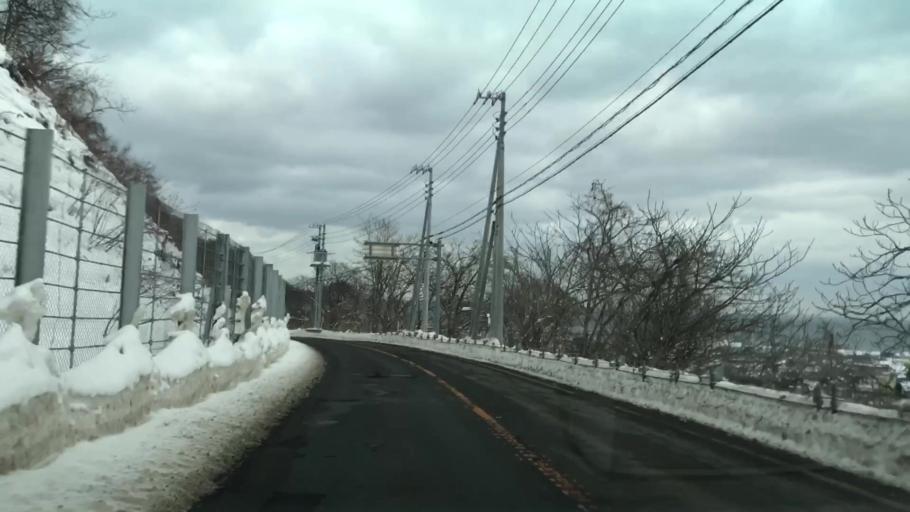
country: JP
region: Hokkaido
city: Yoichi
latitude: 43.2933
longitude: 140.5925
